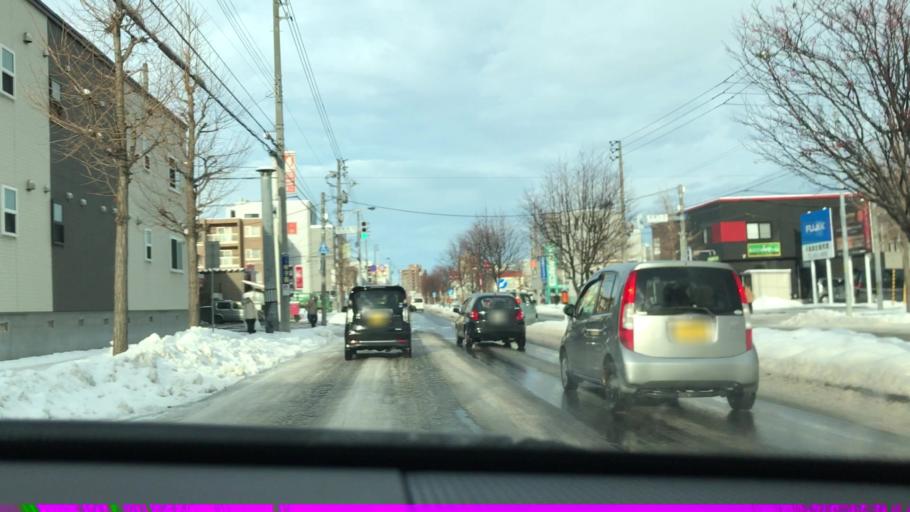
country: JP
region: Hokkaido
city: Sapporo
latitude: 43.0829
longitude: 141.2878
